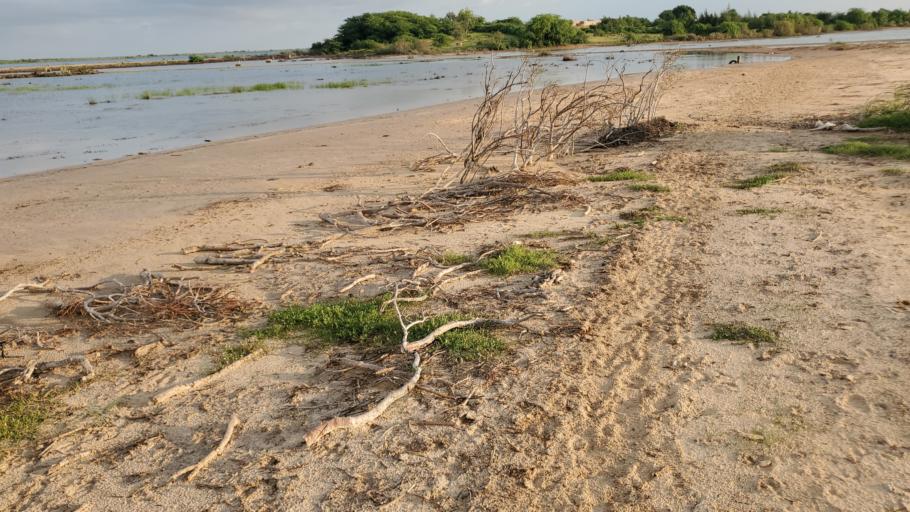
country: SN
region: Saint-Louis
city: Saint-Louis
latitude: 16.0422
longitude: -16.4179
